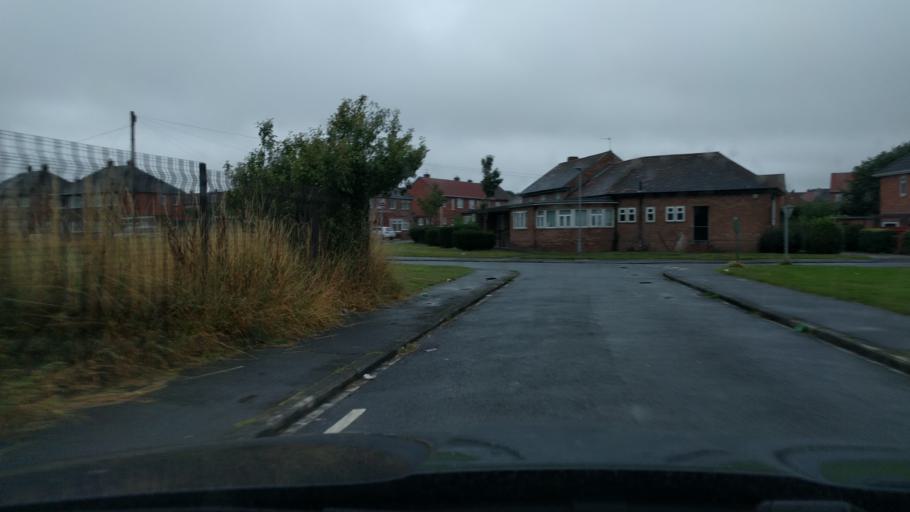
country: GB
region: England
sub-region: Northumberland
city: Bedlington
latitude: 55.1348
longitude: -1.5713
